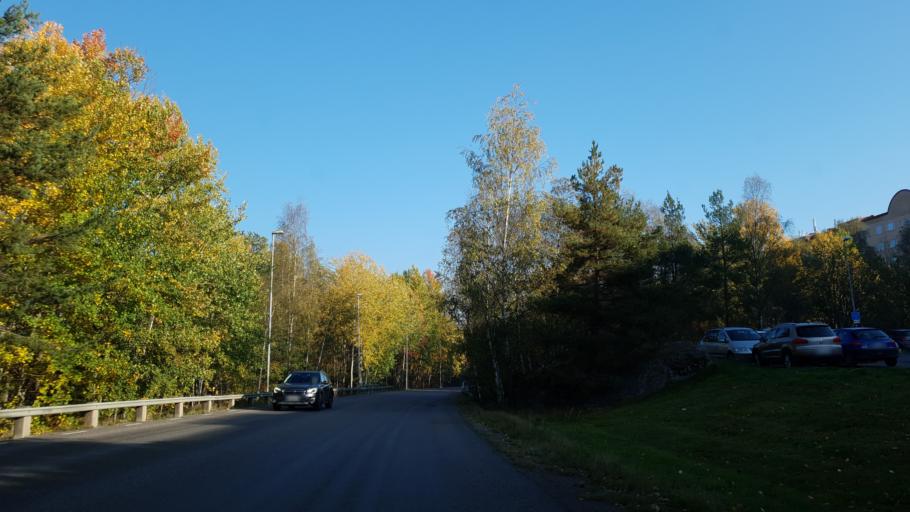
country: SE
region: Stockholm
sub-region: Haninge Kommun
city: Haninge
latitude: 59.1742
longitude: 18.1761
